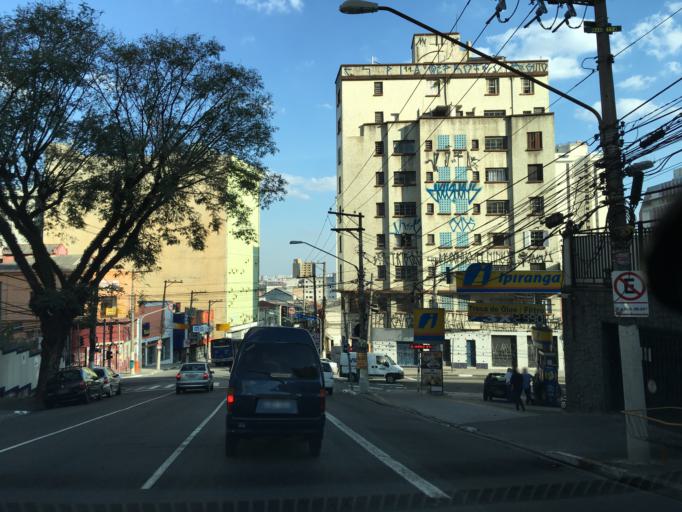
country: BR
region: Sao Paulo
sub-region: Sao Paulo
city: Sao Paulo
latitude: -23.4986
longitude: -46.6257
